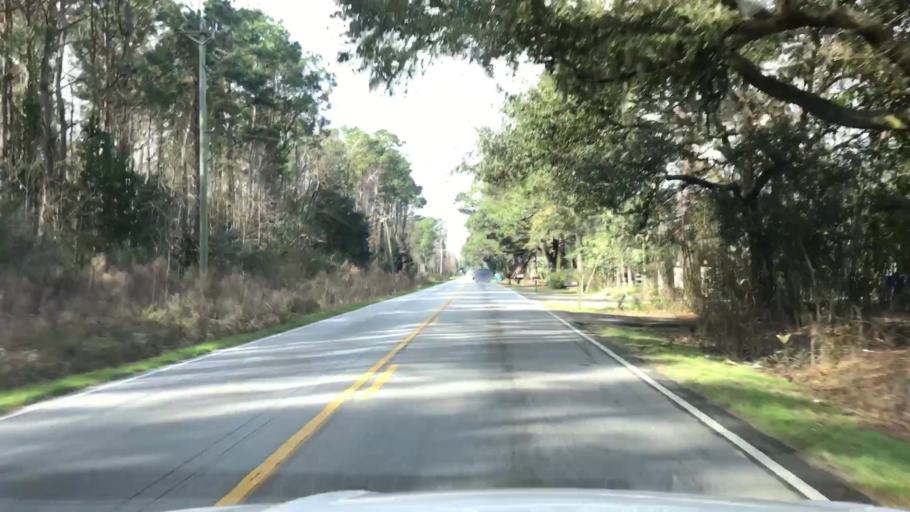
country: US
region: South Carolina
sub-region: Charleston County
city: Shell Point
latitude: 32.7689
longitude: -80.0741
